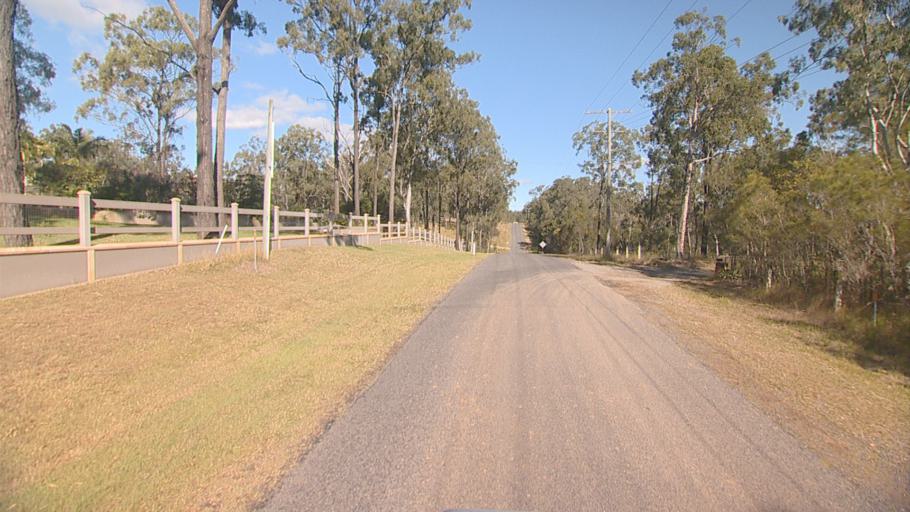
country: AU
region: Queensland
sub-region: Logan
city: Chambers Flat
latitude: -27.8125
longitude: 153.0781
